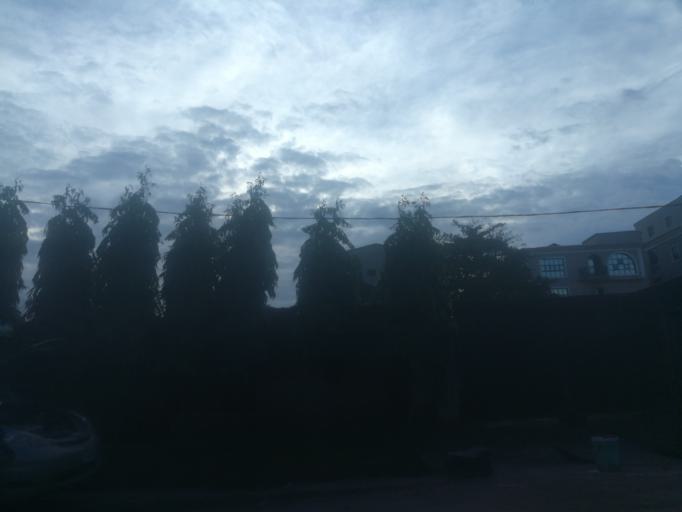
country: NG
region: Lagos
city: Ikeja
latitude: 6.6242
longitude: 3.3569
